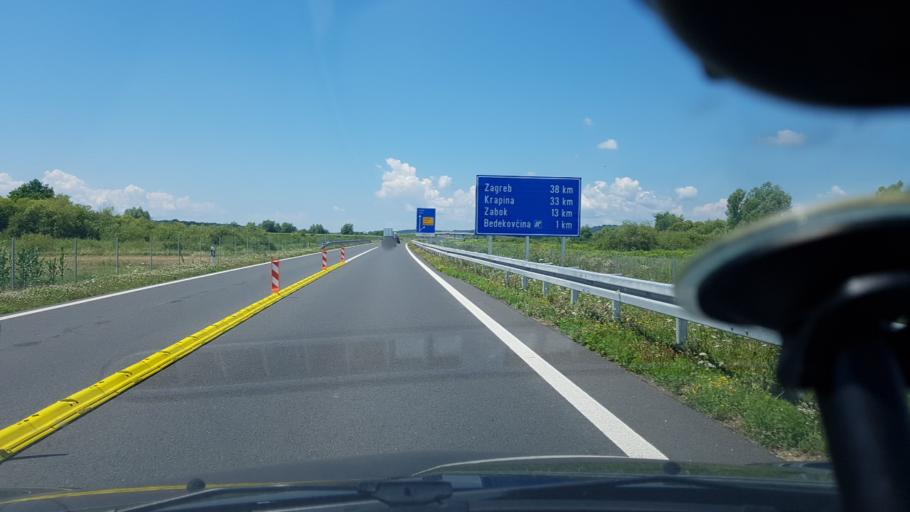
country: HR
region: Krapinsko-Zagorska
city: Bedekovcina
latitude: 46.0363
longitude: 16.0158
